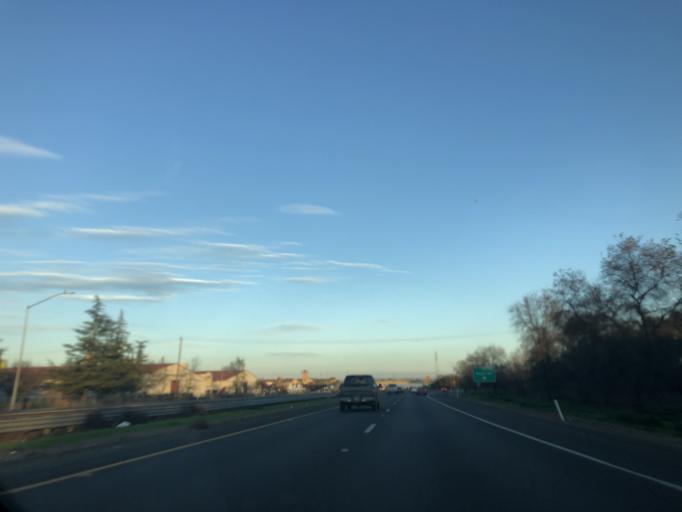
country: US
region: California
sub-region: Yolo County
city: Woodland
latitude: 38.6737
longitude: -121.7346
